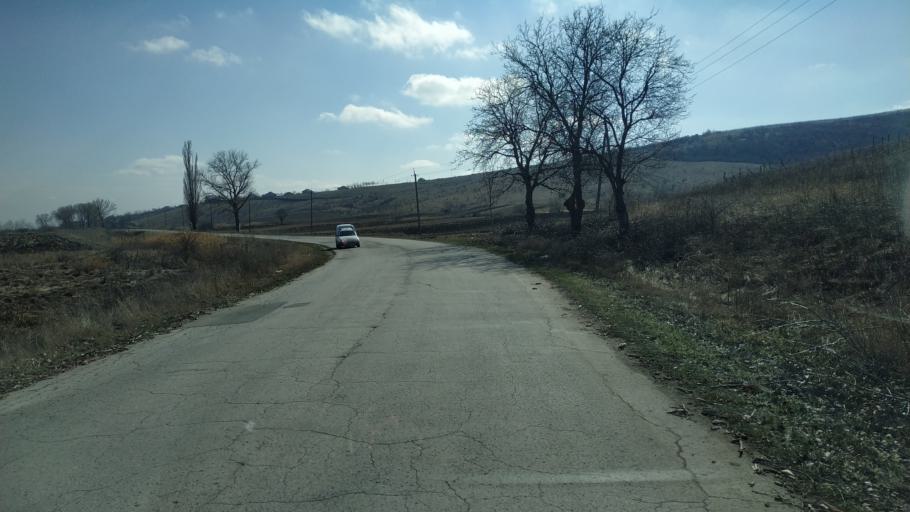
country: MD
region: Hincesti
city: Hincesti
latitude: 46.9425
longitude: 28.6249
